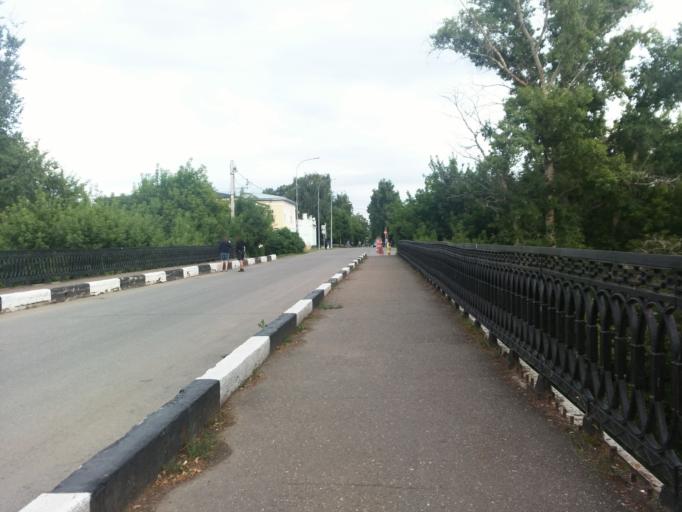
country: RU
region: Tatarstan
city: Yelabuga
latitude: 55.7555
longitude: 52.0629
